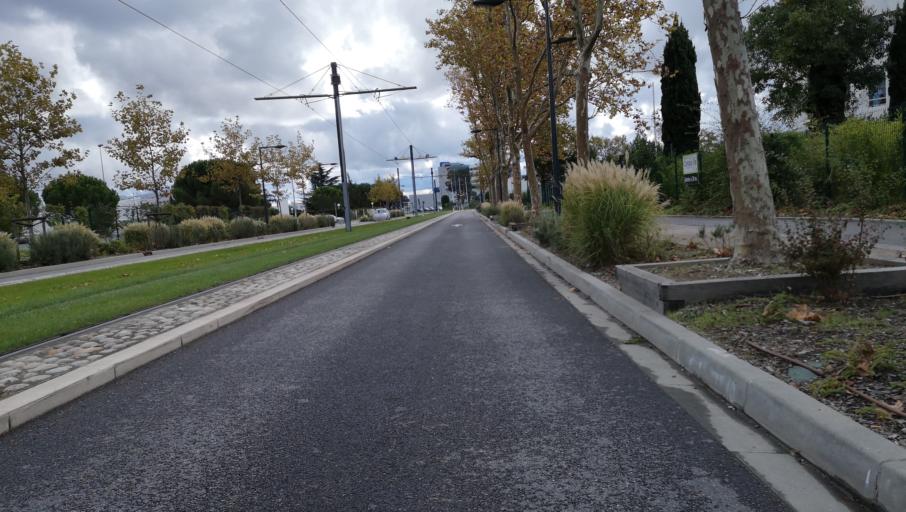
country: FR
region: Midi-Pyrenees
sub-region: Departement de la Haute-Garonne
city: Blagnac
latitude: 43.6270
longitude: 1.3811
